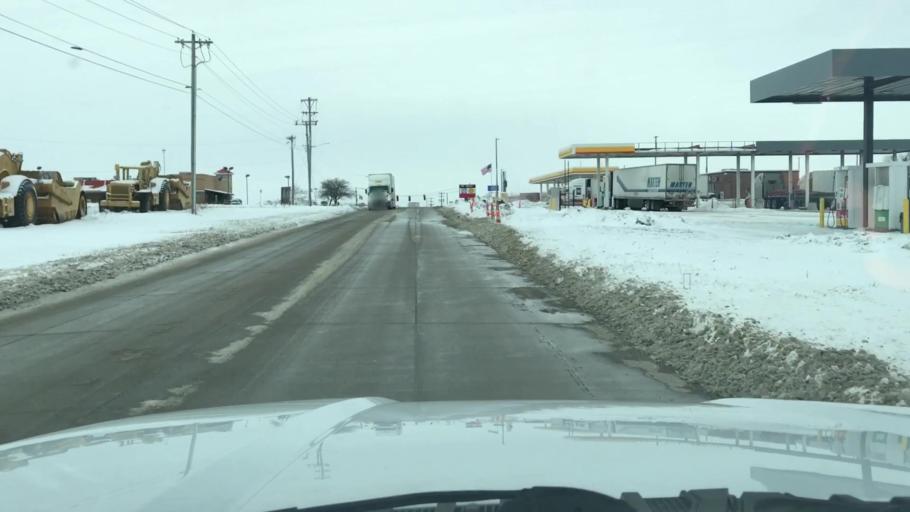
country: US
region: Missouri
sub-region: Clinton County
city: Cameron
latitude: 39.7511
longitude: -94.2154
